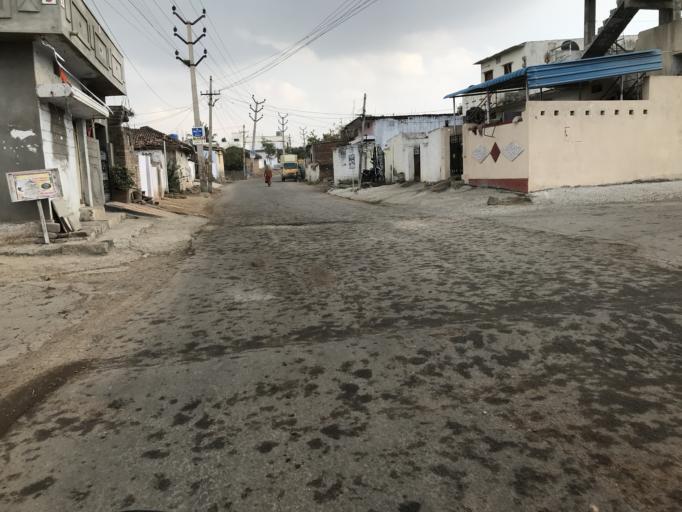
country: IN
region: Telangana
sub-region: Rangareddi
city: Lal Bahadur Nagar
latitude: 17.2851
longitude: 78.6363
